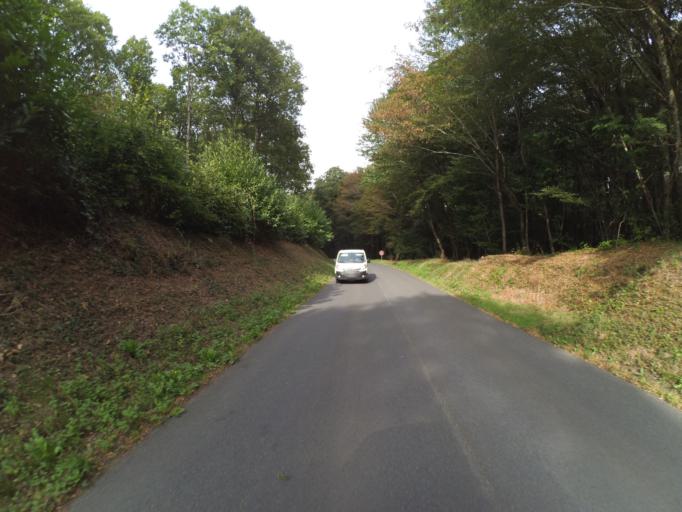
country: FR
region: Centre
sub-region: Departement d'Indre-et-Loire
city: Reugny
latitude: 47.4808
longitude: 0.8974
